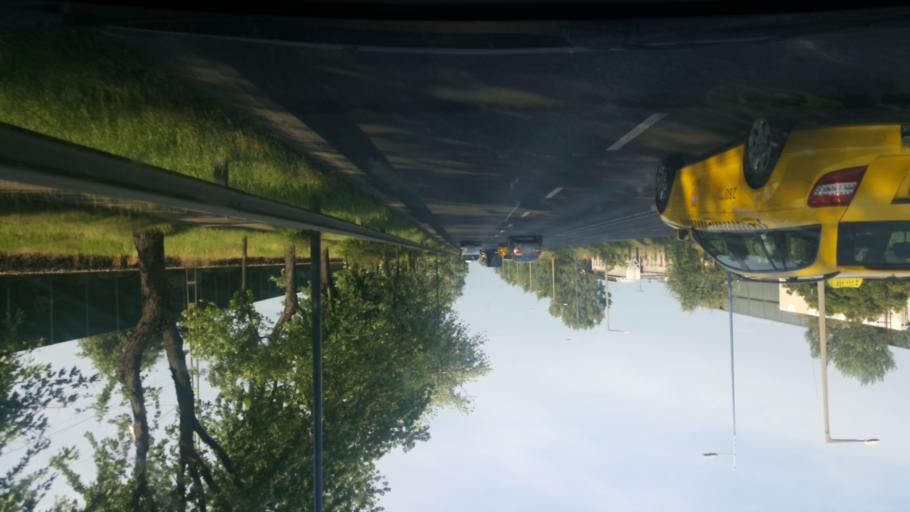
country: HU
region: Pest
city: Gyal
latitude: 47.4320
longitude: 19.2302
